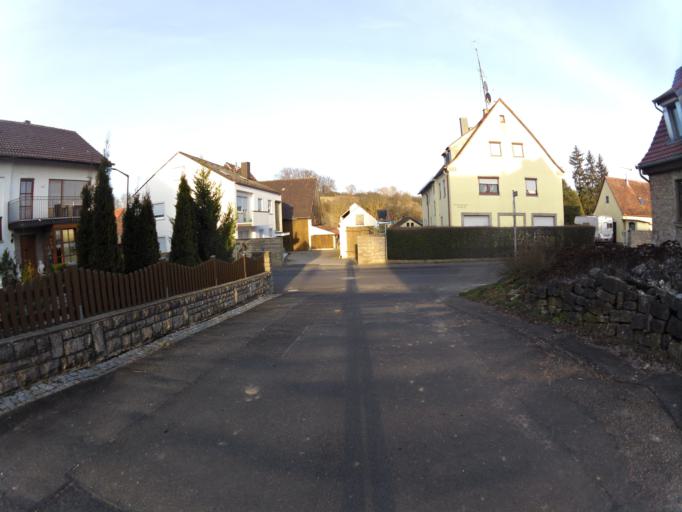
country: DE
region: Bavaria
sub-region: Regierungsbezirk Unterfranken
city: Prosselsheim
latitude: 49.8383
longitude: 10.1471
